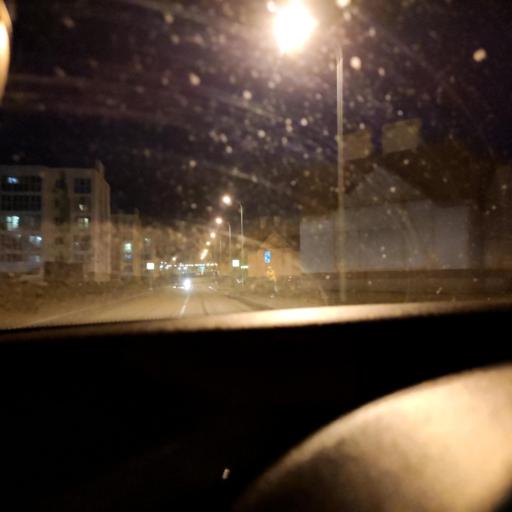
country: RU
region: Samara
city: Petra-Dubrava
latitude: 53.2955
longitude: 50.3204
